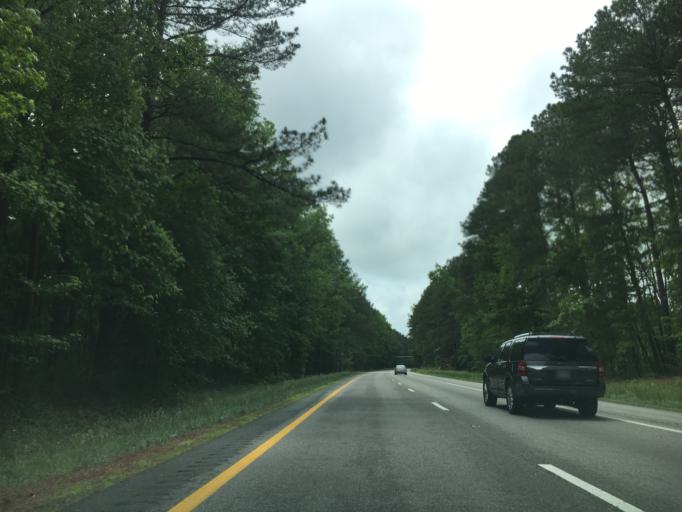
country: US
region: Virginia
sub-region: Brunswick County
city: Lawrenceville
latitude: 36.8505
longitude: -77.8714
